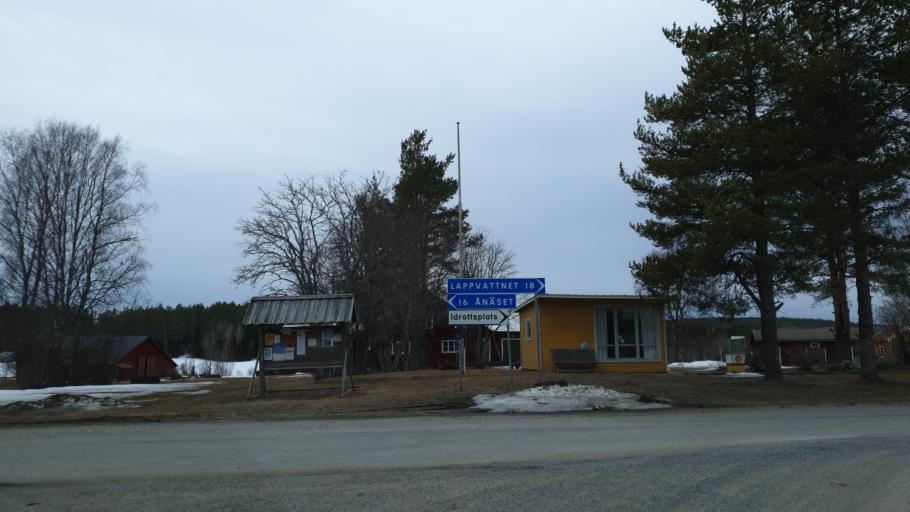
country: SE
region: Vaesterbotten
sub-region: Robertsfors Kommun
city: Robertsfors
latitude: 64.4030
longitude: 21.0086
